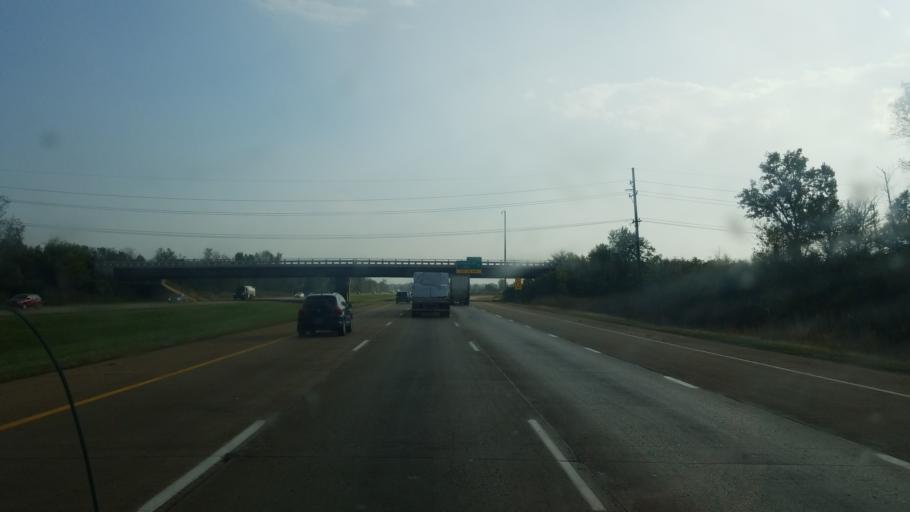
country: US
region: Michigan
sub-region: Monroe County
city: Carleton
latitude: 42.1387
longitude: -83.3822
